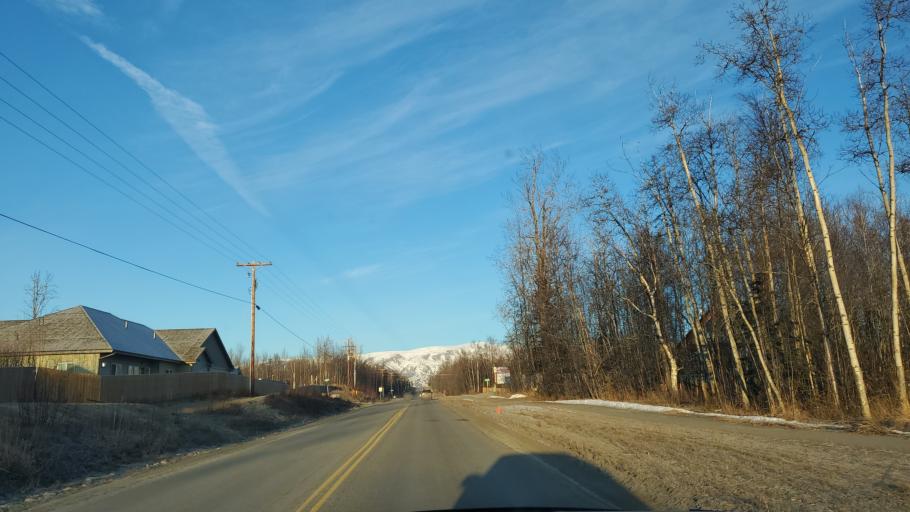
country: US
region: Alaska
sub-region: Matanuska-Susitna Borough
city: Wasilla
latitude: 61.5912
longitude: -149.4508
